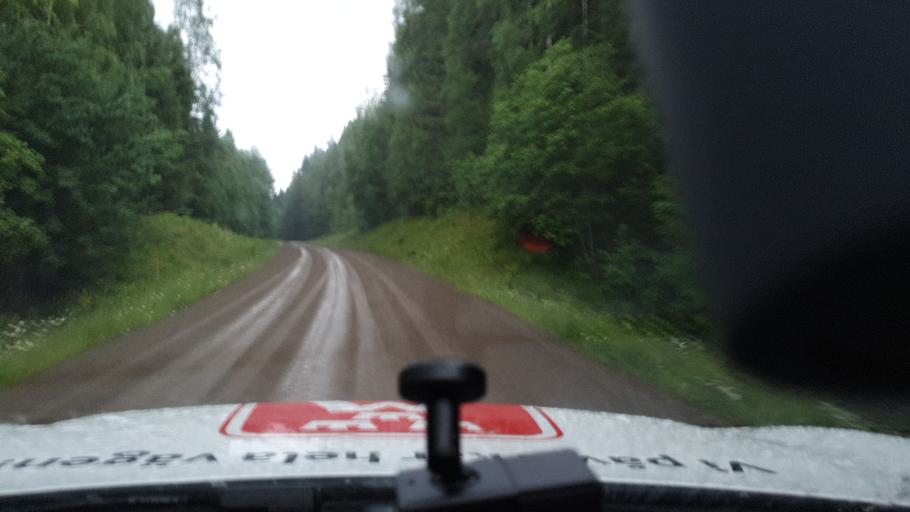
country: SE
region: Vaermland
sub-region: Hagfors Kommun
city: Ekshaerad
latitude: 60.4224
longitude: 13.2457
